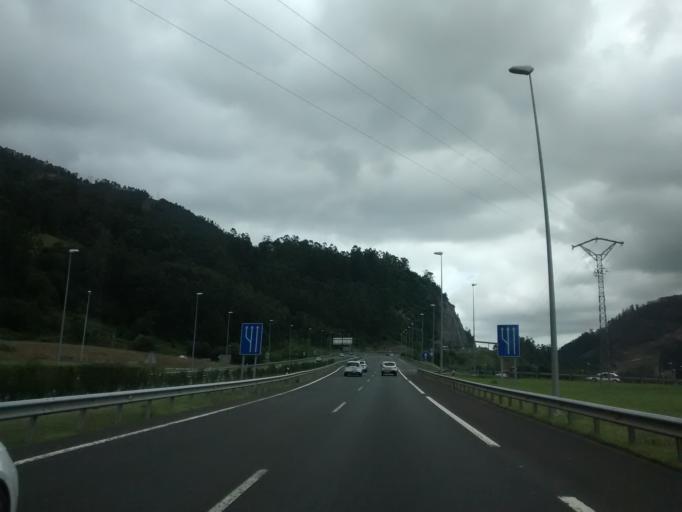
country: ES
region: Cantabria
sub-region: Provincia de Cantabria
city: Los Corrales de Buelna
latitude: 43.2837
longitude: -4.0813
